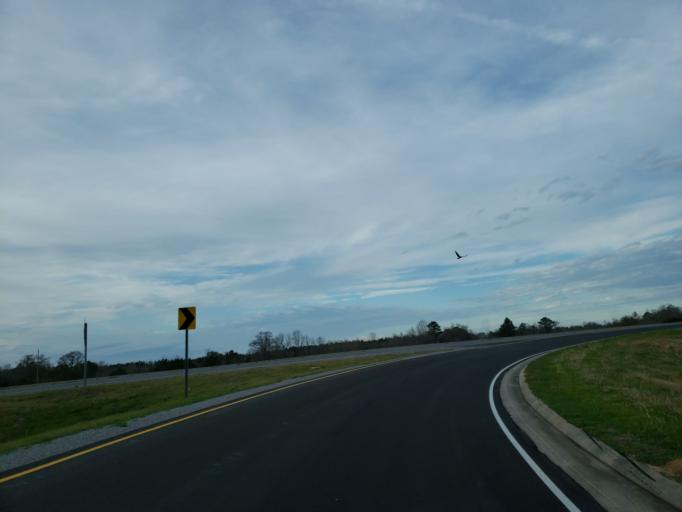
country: US
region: Mississippi
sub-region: Clarke County
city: Quitman
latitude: 31.9777
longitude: -88.7217
